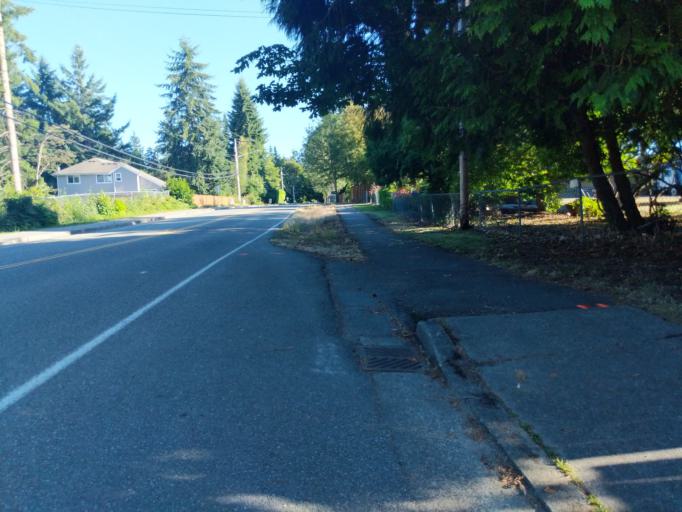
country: US
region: Washington
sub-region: King County
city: Bothell
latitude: 47.7789
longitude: -122.2019
